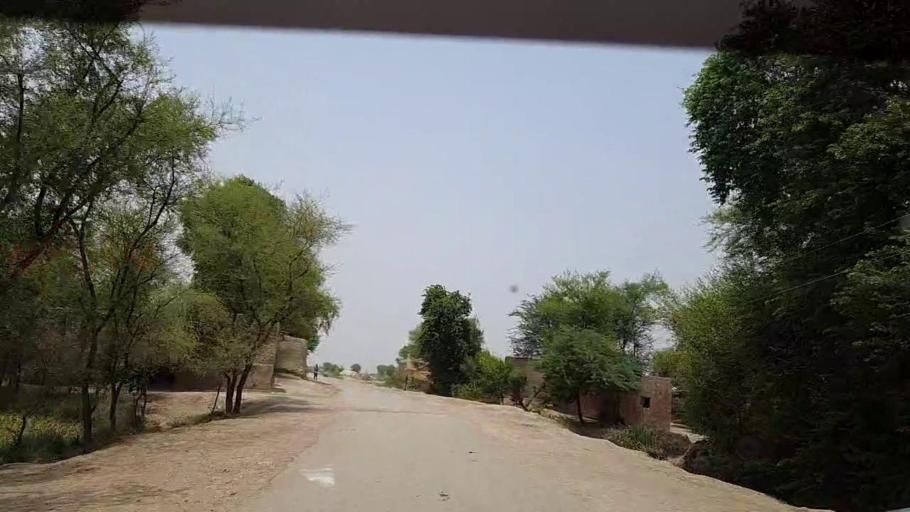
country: PK
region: Sindh
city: Khairpur Nathan Shah
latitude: 27.0219
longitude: 67.6693
